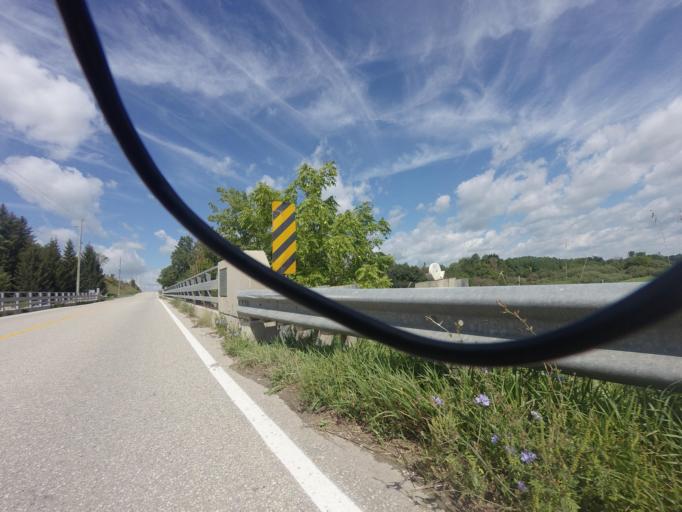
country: CA
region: Ontario
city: Stratford
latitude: 43.5158
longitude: -80.8434
